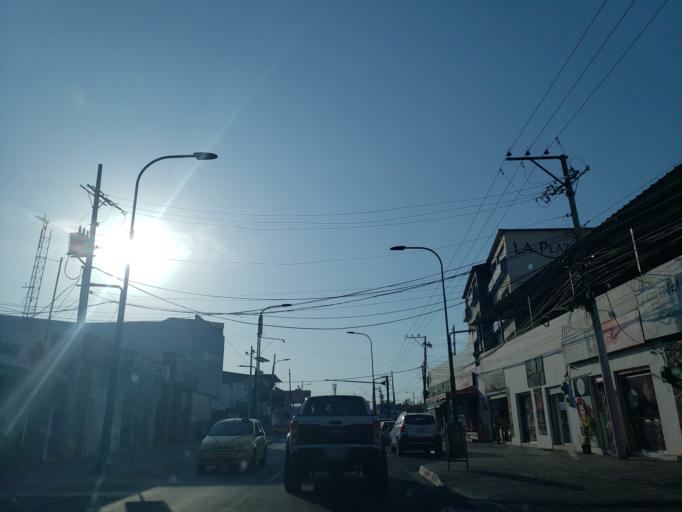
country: EC
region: Manabi
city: Manta
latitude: -0.9448
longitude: -80.7332
